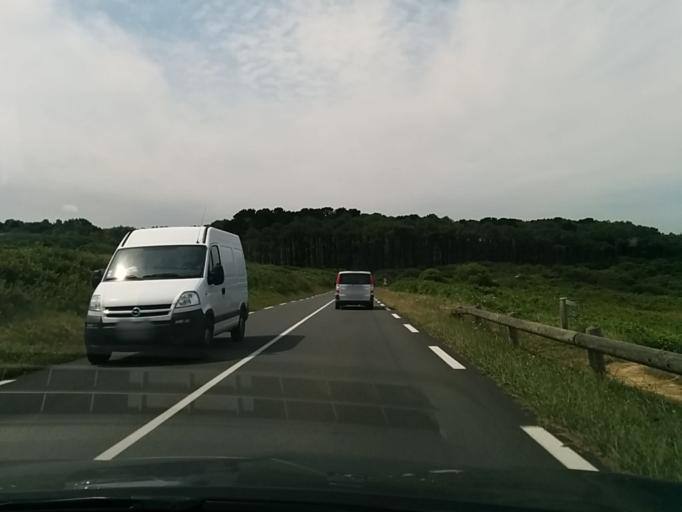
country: FR
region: Aquitaine
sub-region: Departement des Pyrenees-Atlantiques
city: Urrugne
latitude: 43.3834
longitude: -1.7262
